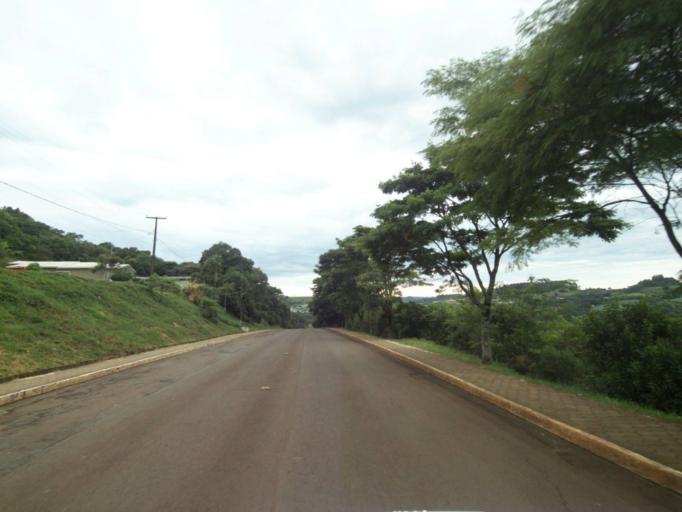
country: BR
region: Parana
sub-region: Guaraniacu
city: Guaraniacu
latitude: -25.1056
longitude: -52.8592
